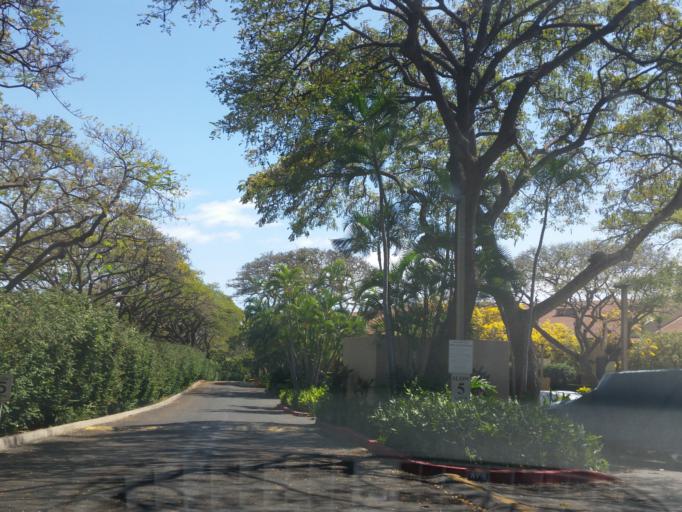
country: US
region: Hawaii
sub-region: Maui County
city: Ka'anapali
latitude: 20.9232
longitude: -156.6903
